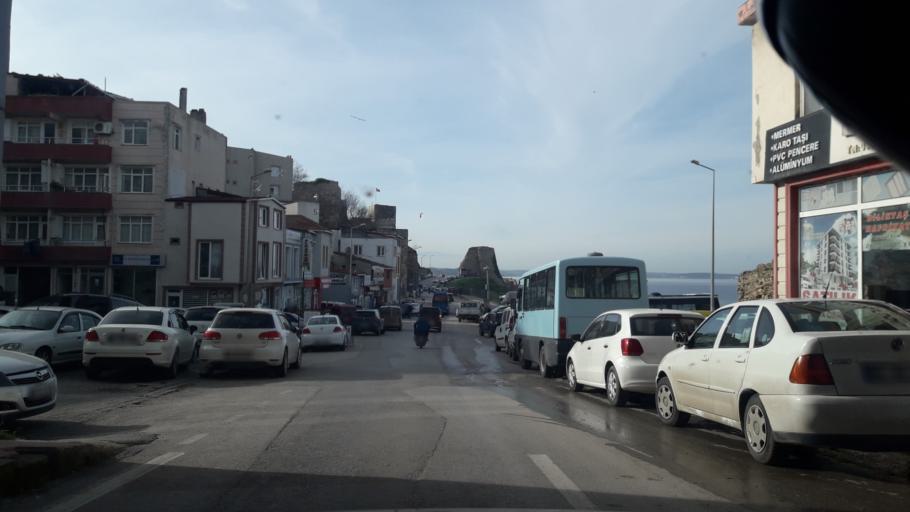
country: TR
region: Sinop
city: Sinop
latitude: 42.0265
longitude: 35.1450
